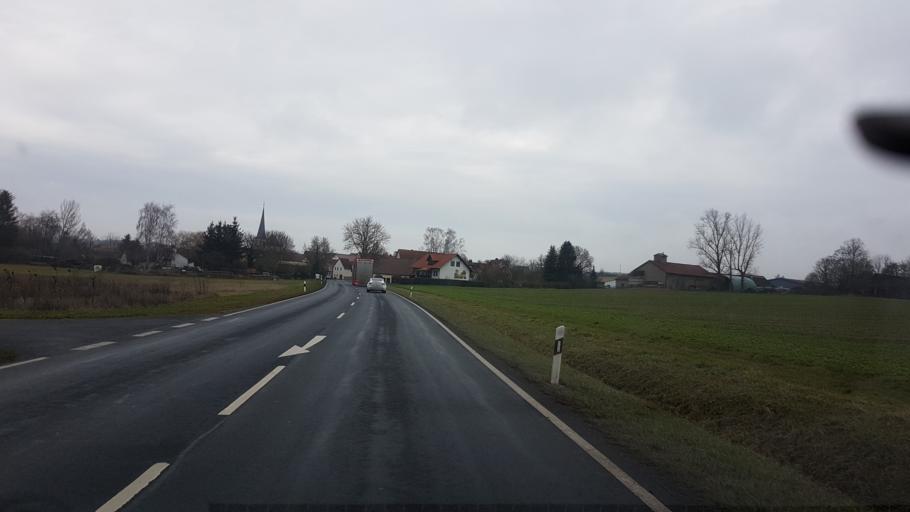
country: DE
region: Bavaria
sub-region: Regierungsbezirk Unterfranken
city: Bad Konigshofen im Grabfeld
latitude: 50.2766
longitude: 10.5233
